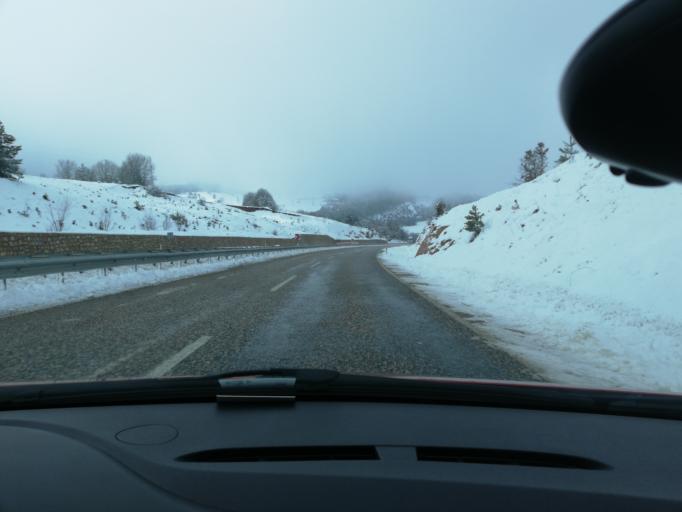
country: TR
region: Kastamonu
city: Akkaya
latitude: 41.2828
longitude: 33.4678
